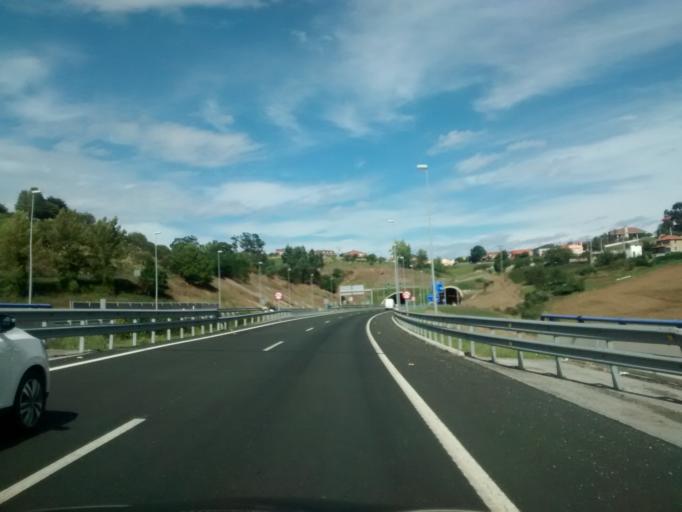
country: ES
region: Cantabria
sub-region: Provincia de Cantabria
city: Camargo
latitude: 43.3890
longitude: -3.8651
